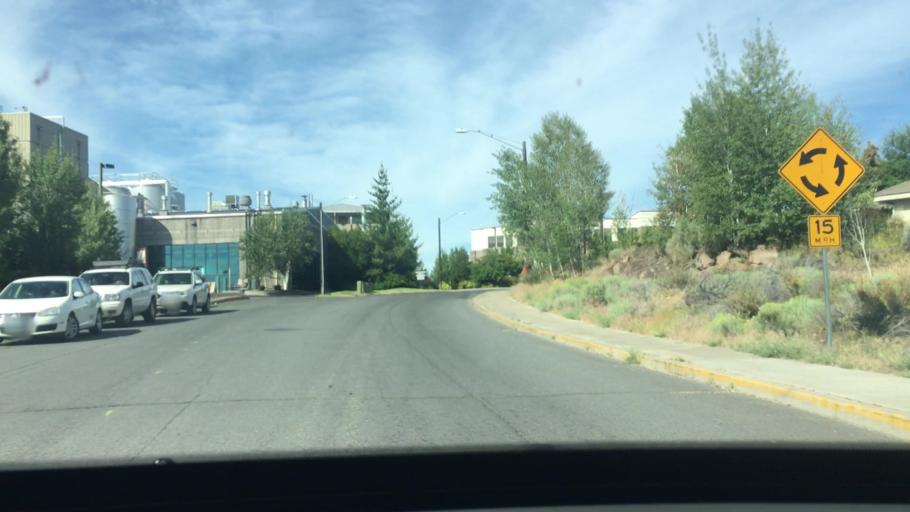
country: US
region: Oregon
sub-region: Deschutes County
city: Bend
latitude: 44.0480
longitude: -121.3215
